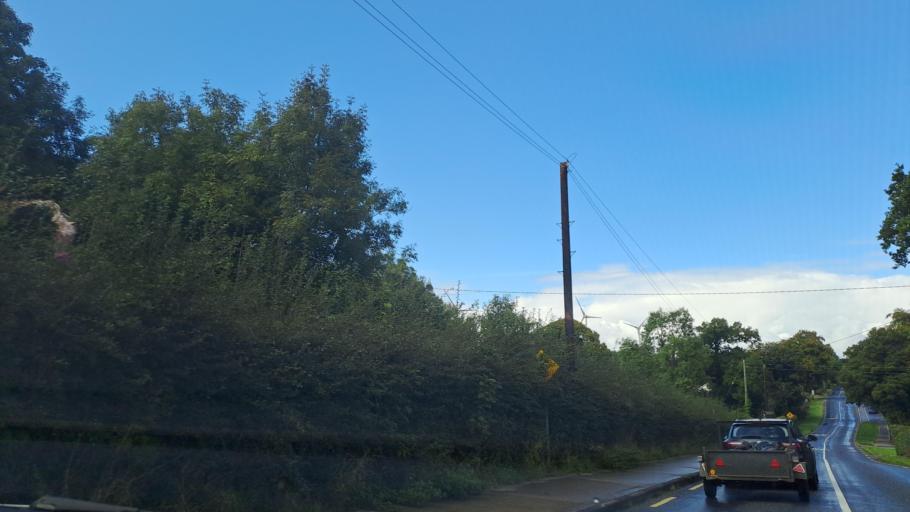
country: IE
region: Ulster
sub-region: An Cabhan
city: Kingscourt
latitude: 53.9179
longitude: -6.8101
